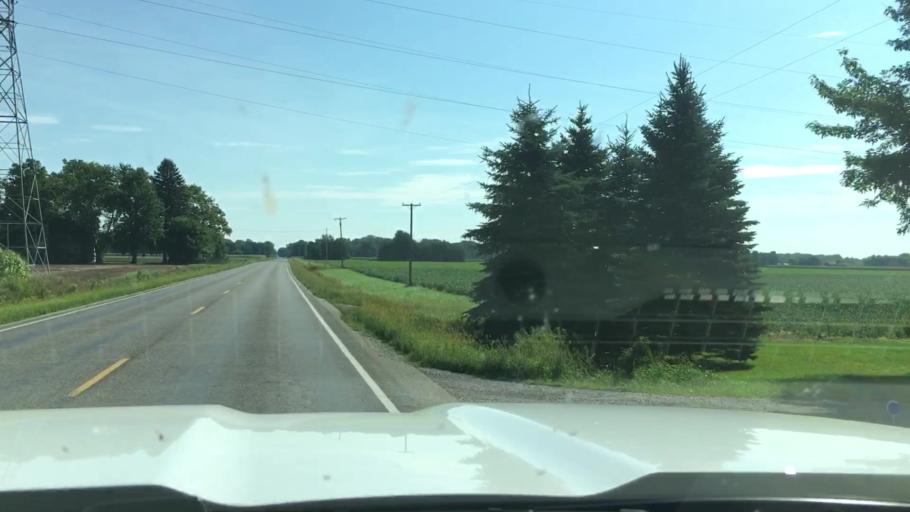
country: US
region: Michigan
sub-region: Saginaw County
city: Freeland
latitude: 43.5253
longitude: -84.1804
